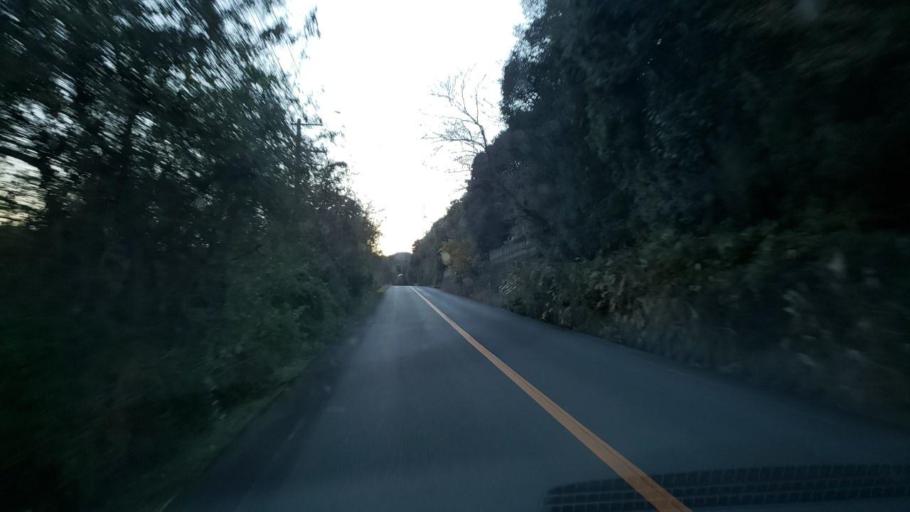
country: JP
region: Hyogo
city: Fukura
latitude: 34.2947
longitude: 134.7258
